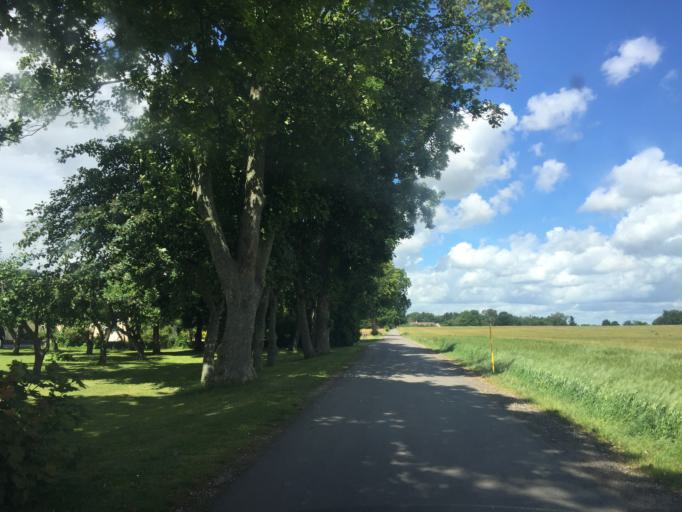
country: DK
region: Capital Region
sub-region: Hoje-Taastrup Kommune
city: Taastrup
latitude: 55.6990
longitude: 12.2700
